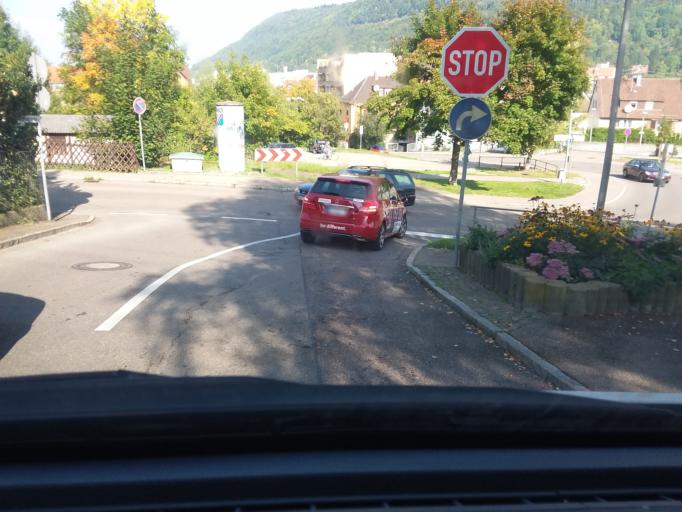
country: DE
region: Baden-Wuerttemberg
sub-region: Regierungsbezirk Stuttgart
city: Geislingen an der Steige
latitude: 48.6220
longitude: 9.8288
